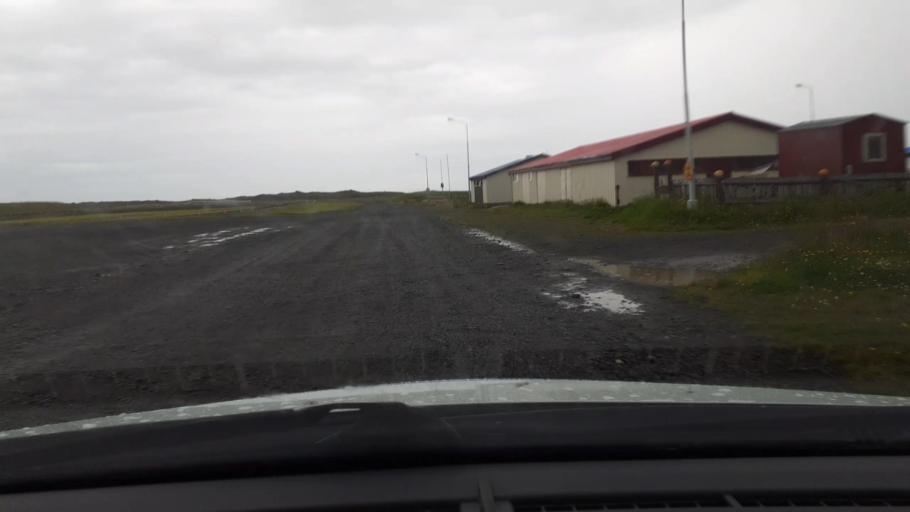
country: IS
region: West
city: Akranes
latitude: 64.3397
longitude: -22.0246
